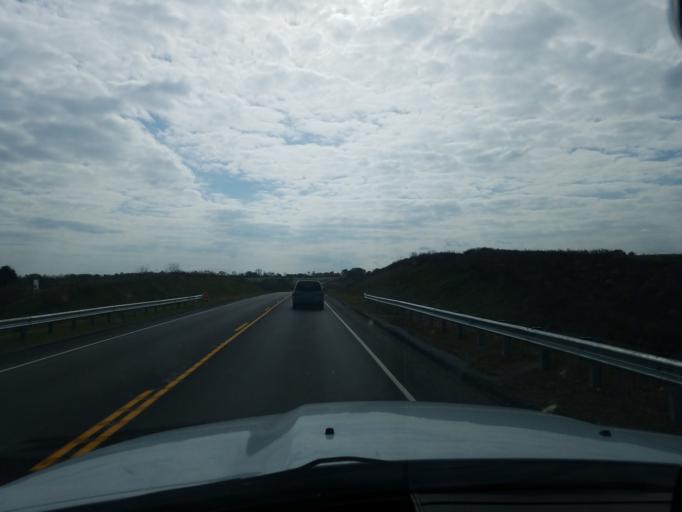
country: US
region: Kentucky
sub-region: Bullitt County
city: Mount Washington
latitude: 37.9475
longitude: -85.4670
